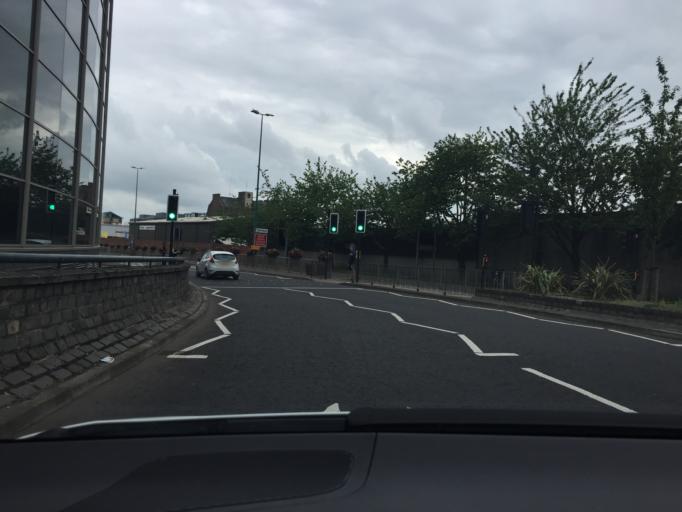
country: GB
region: Scotland
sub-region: Dundee City
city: Dundee
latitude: 56.4639
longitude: -2.9639
